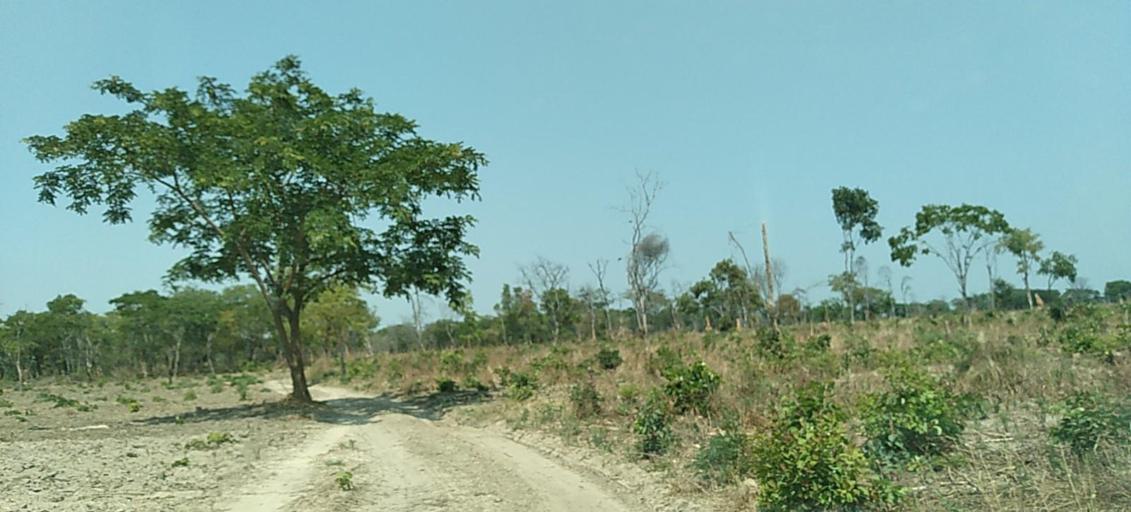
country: ZM
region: Copperbelt
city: Mpongwe
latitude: -13.8692
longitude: 28.0511
